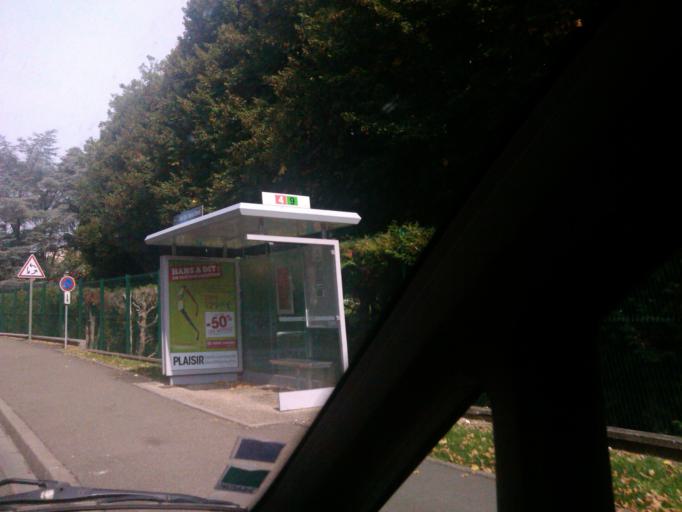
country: FR
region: Ile-de-France
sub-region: Departement des Yvelines
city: Plaisir
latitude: 48.8243
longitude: 1.9451
